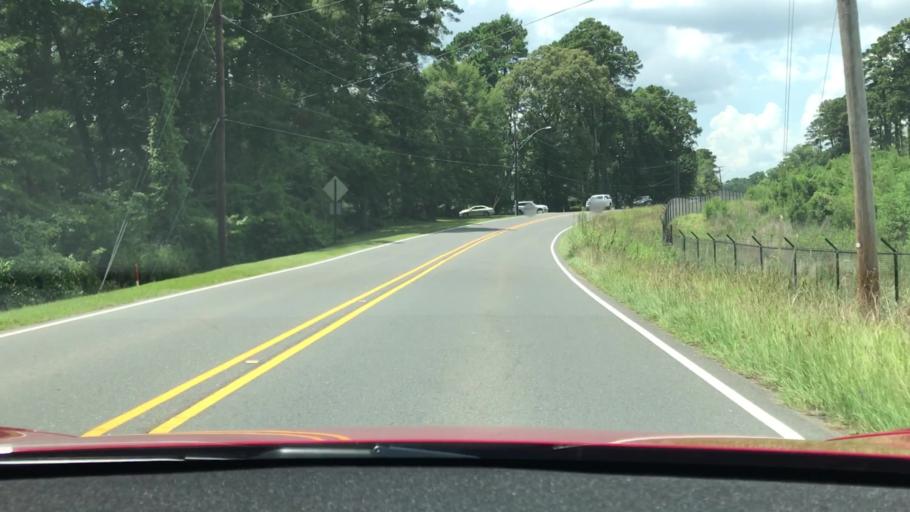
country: US
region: Louisiana
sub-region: Bossier Parish
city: Bossier City
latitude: 32.3851
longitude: -93.7161
